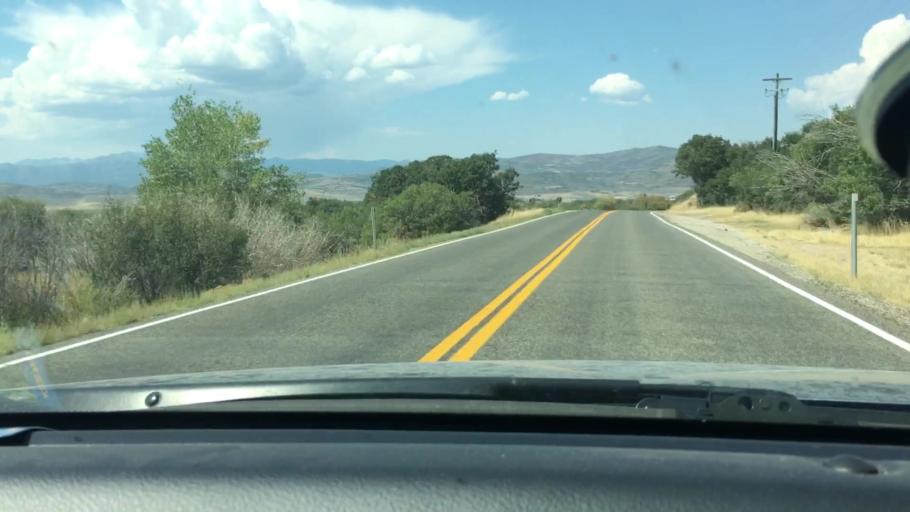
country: US
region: Utah
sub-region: Summit County
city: Kamas
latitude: 40.6405
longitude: -111.2639
